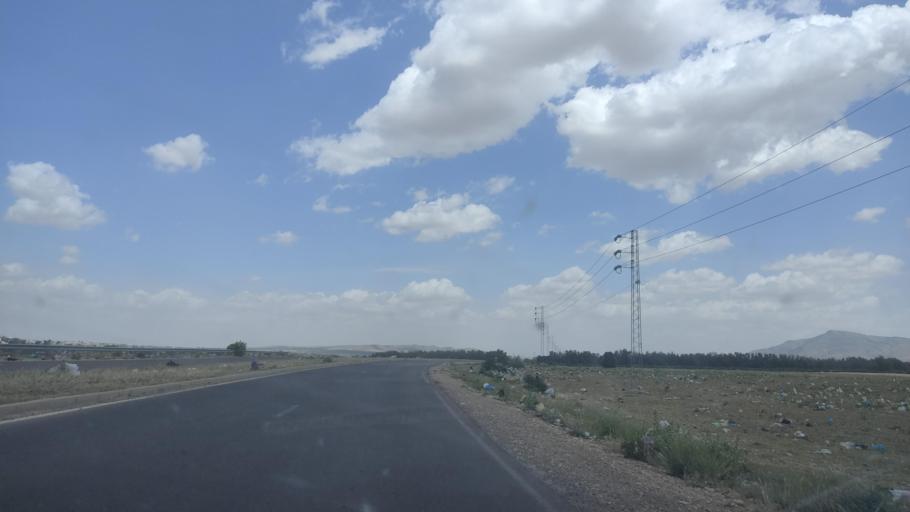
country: TN
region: Al Qasrayn
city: Kasserine
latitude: 35.1993
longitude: 8.8617
